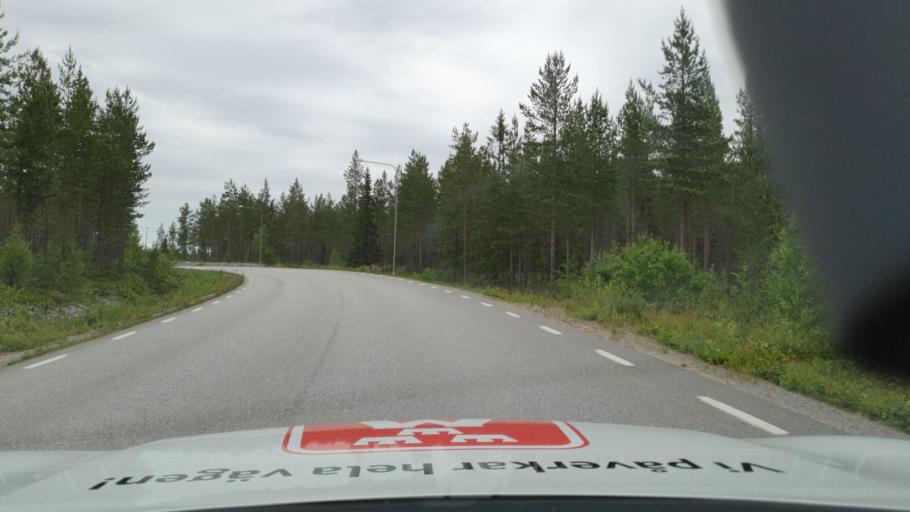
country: SE
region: Vaesterbotten
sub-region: Nordmalings Kommun
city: Nordmaling
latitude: 63.5342
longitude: 19.4050
